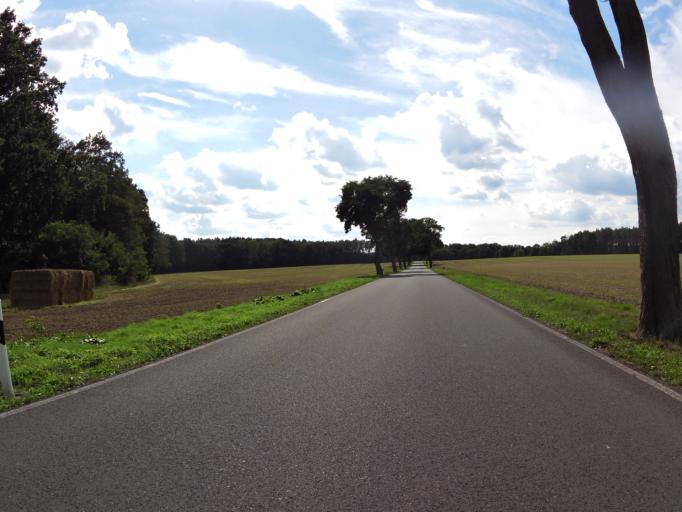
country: DE
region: Brandenburg
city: Munchehofe
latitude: 52.2065
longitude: 13.8658
